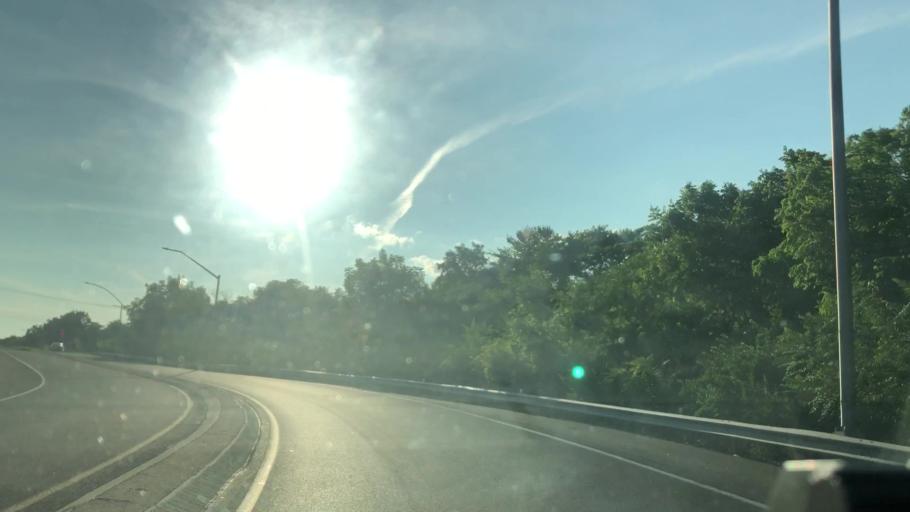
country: US
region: Pennsylvania
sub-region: Northampton County
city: Bethlehem
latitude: 40.6295
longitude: -75.3928
